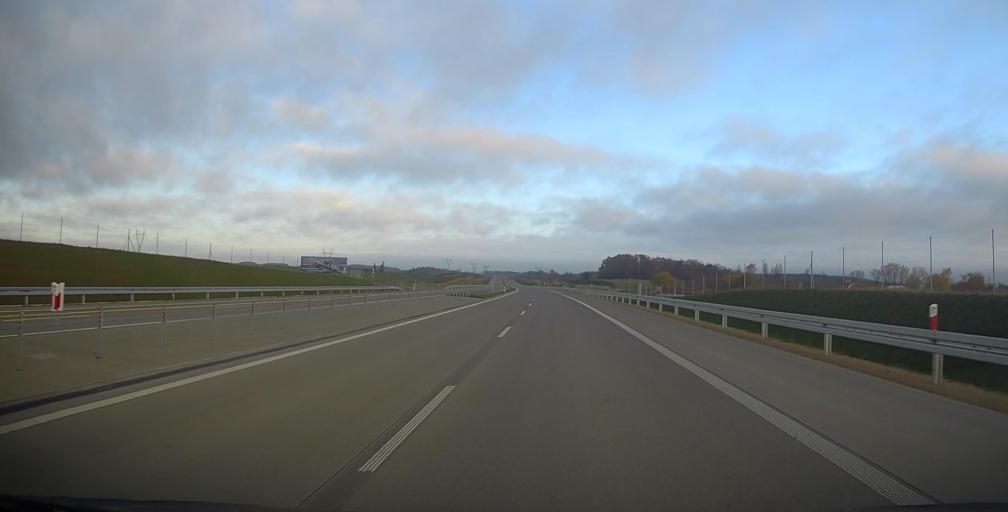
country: PL
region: Podlasie
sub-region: Powiat grajewski
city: Szczuczyn
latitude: 53.6614
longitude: 22.2987
